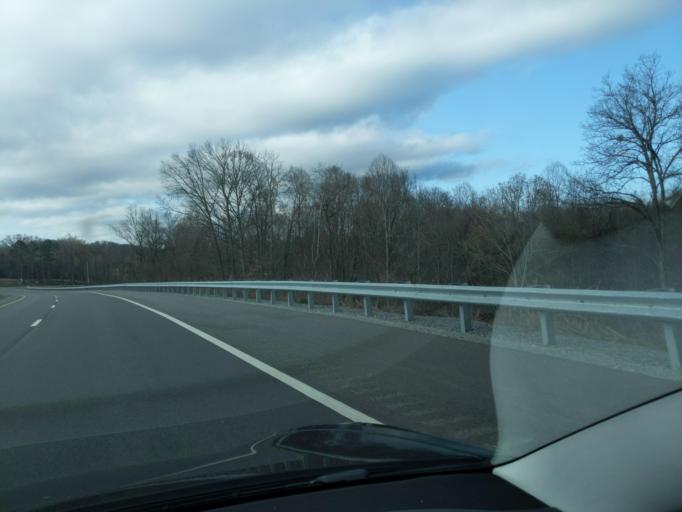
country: US
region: Tennessee
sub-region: Hamblen County
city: Morristown
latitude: 36.1630
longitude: -83.3446
